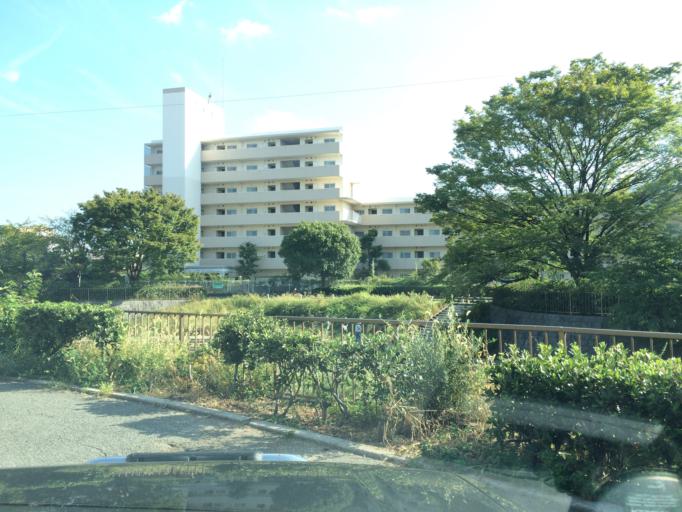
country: JP
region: Hyogo
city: Amagasaki
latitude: 34.7485
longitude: 135.4066
